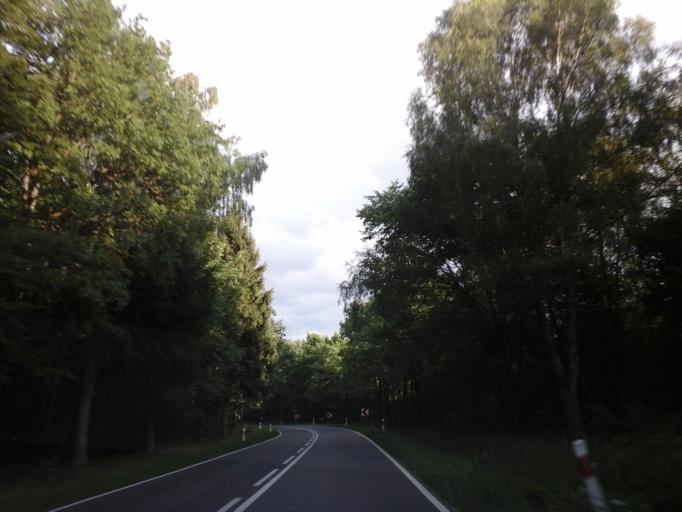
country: PL
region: West Pomeranian Voivodeship
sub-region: Powiat kamienski
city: Golczewo
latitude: 53.8777
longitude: 14.8915
